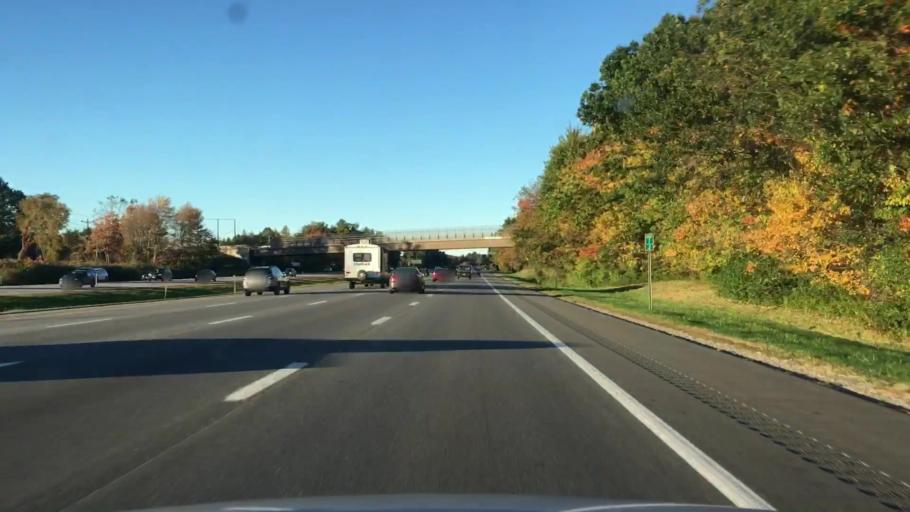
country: US
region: New Hampshire
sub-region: Rockingham County
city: North Hampton
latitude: 42.9823
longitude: -70.8520
